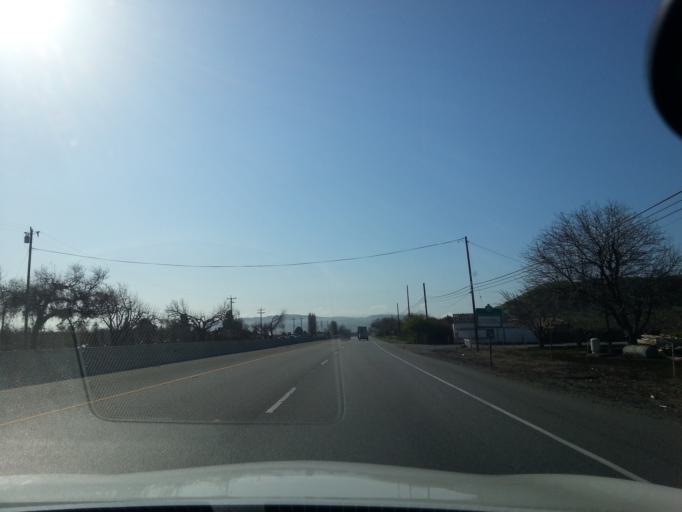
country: US
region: California
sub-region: Santa Clara County
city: Gilroy
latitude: 36.9740
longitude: -121.5548
